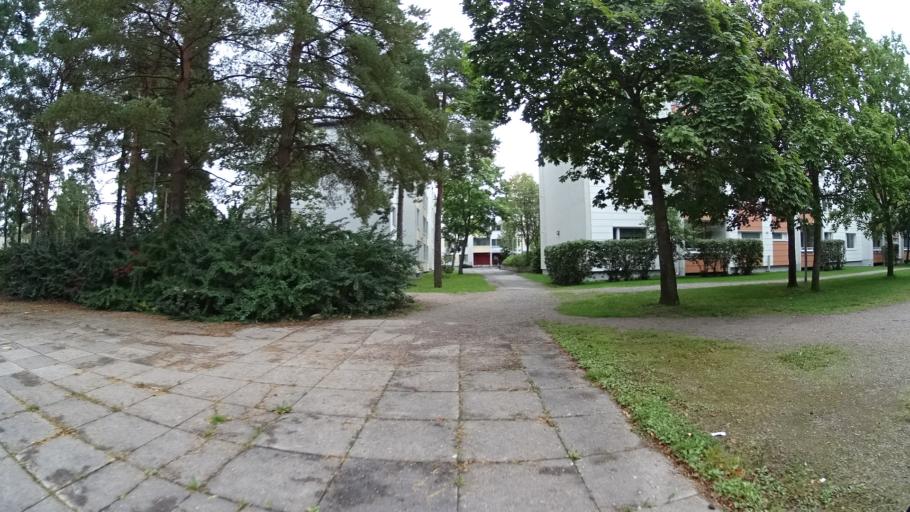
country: FI
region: Uusimaa
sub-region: Helsinki
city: Espoo
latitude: 60.1488
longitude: 24.6505
